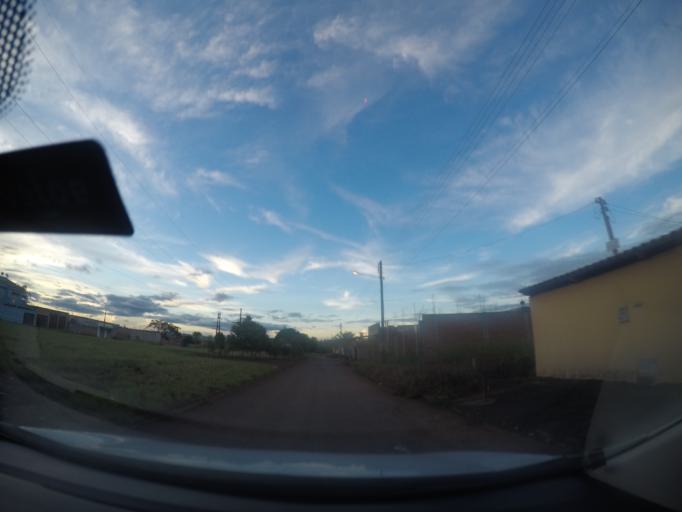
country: BR
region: Goias
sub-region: Goianira
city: Goianira
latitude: -16.5723
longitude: -49.3818
